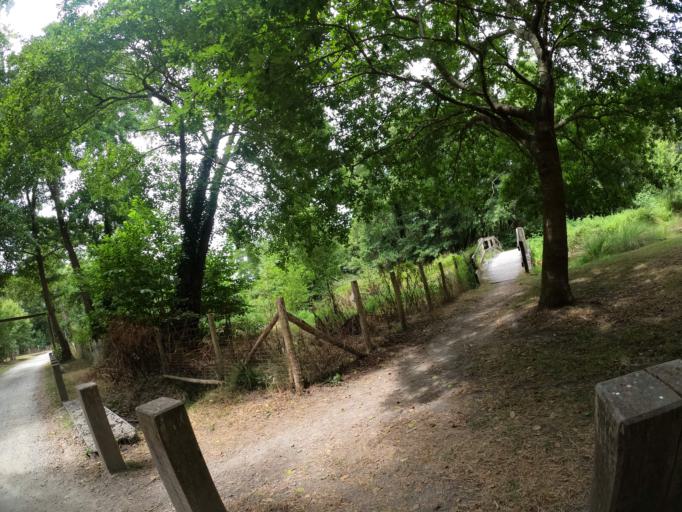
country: FR
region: Aquitaine
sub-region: Departement des Landes
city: Leon
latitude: 43.8873
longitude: -1.3125
